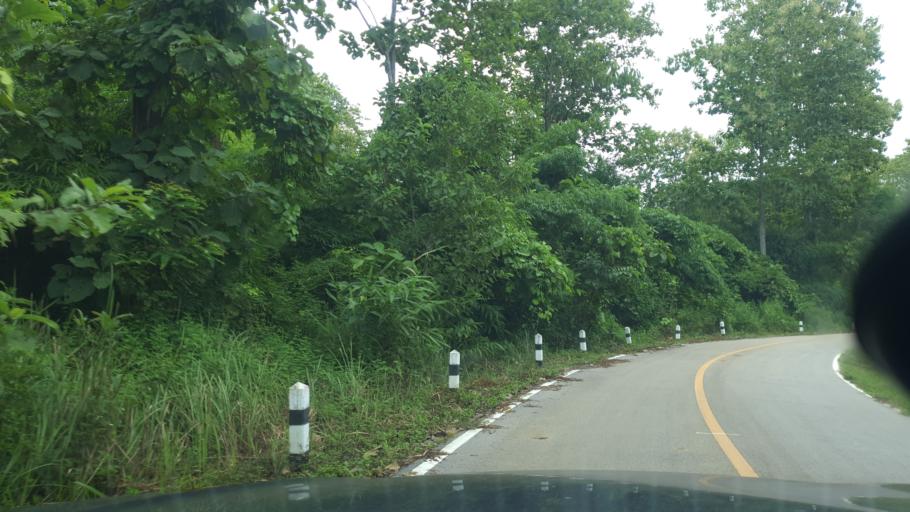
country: TH
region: Lampang
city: Hang Chat
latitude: 18.3763
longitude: 99.2594
